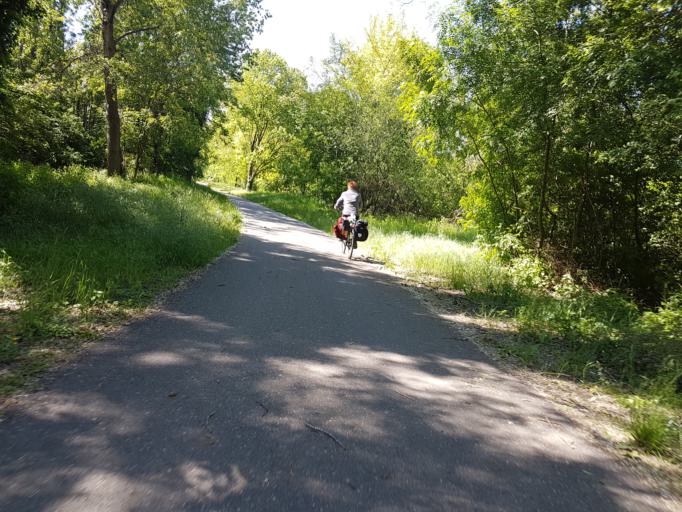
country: FR
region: Rhone-Alpes
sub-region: Departement de la Drome
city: Andancette
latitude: 45.2658
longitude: 4.8122
